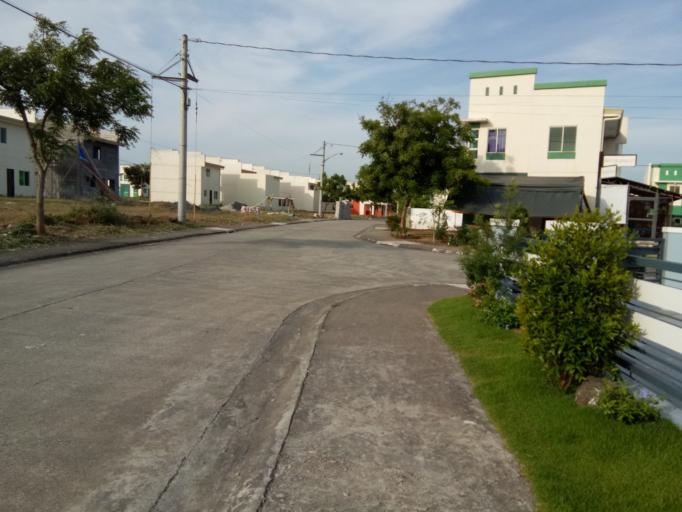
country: PH
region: Calabarzon
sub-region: Province of Cavite
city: Biga
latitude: 14.2768
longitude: 120.9687
